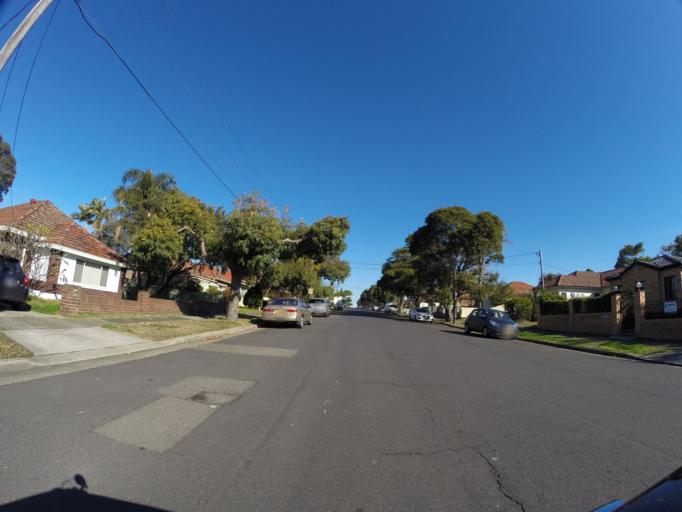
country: AU
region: New South Wales
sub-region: Auburn
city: Lidcombe
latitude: -33.8538
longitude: 151.0577
